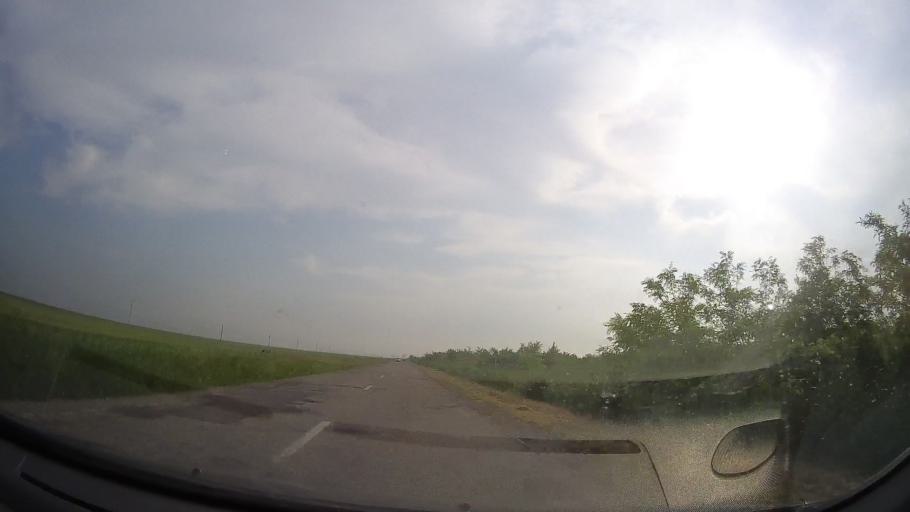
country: RO
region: Timis
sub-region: Comuna Giulvaz
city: Giulvaz
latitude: 45.5695
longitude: 21.0072
